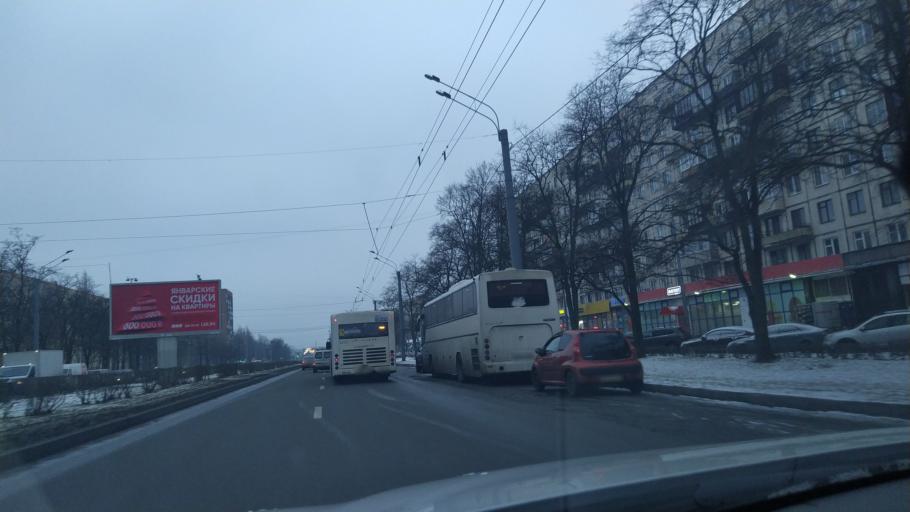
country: RU
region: St.-Petersburg
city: Grazhdanka
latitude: 60.0368
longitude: 30.3963
